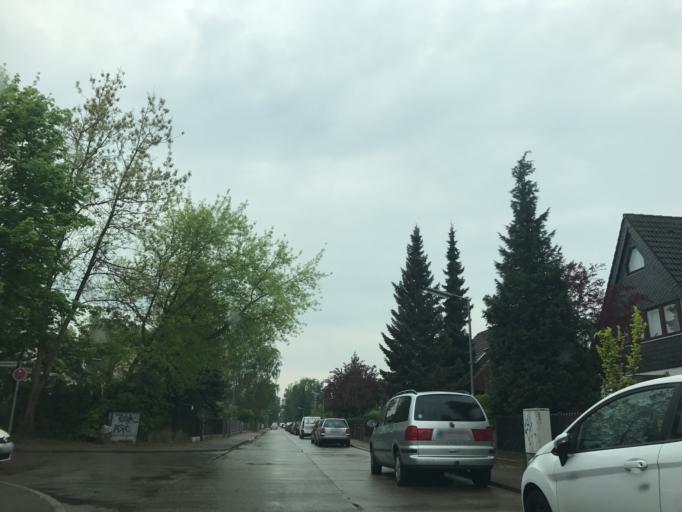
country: DE
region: Berlin
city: Staaken
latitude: 52.5528
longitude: 13.1517
